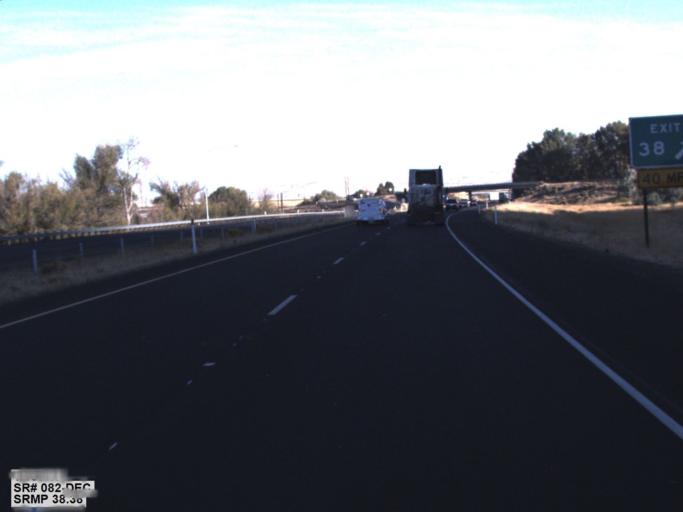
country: US
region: Washington
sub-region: Yakima County
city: Union Gap
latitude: 46.5329
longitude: -120.4716
